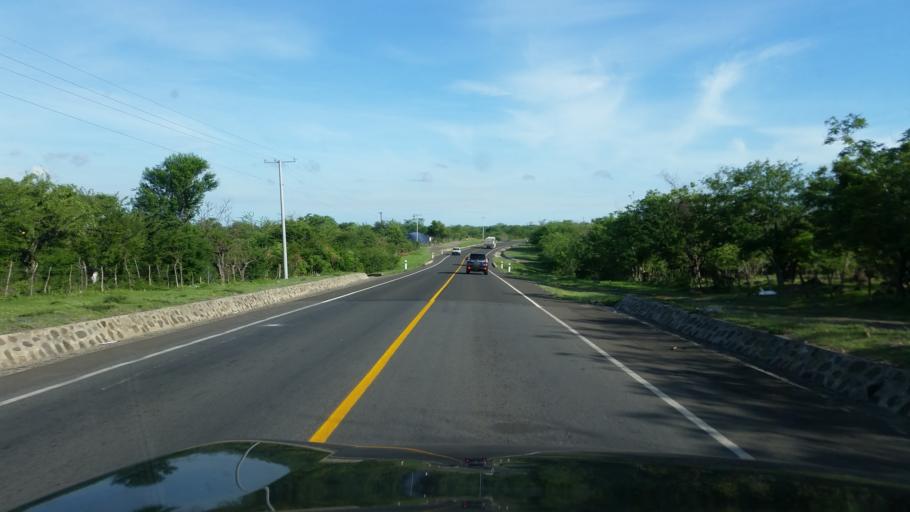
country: NI
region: Leon
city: La Paz Centro
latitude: 12.2455
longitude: -86.7186
